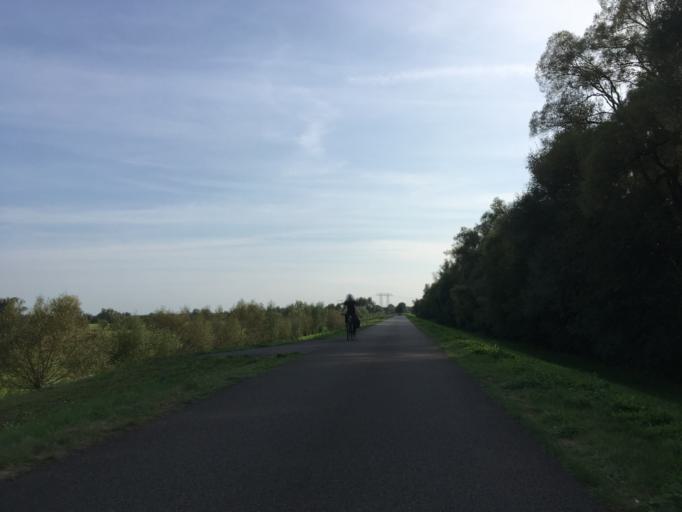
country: DE
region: Brandenburg
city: Brieskow-Finkenheerd
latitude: 52.2688
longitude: 14.5852
